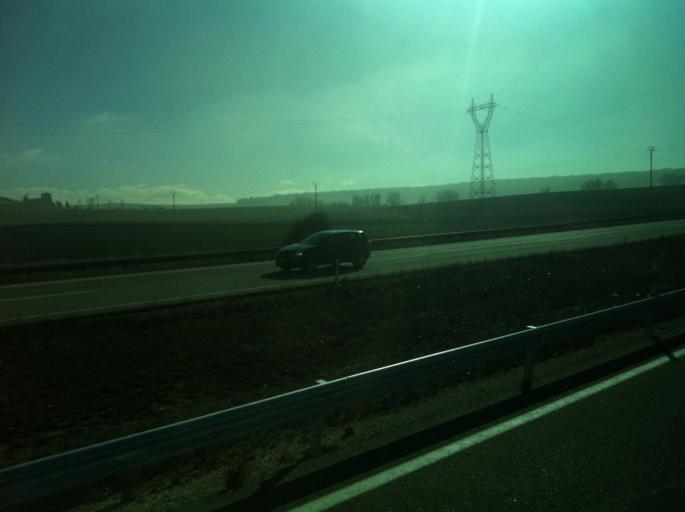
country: ES
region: Castille and Leon
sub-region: Provincia de Burgos
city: Rubena
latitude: 42.3648
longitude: -3.5911
